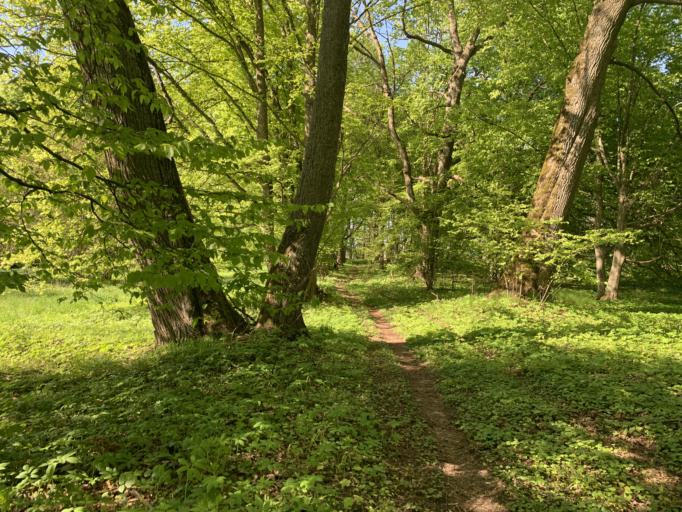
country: BY
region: Minsk
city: Kapyl'
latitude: 53.2598
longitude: 26.9494
